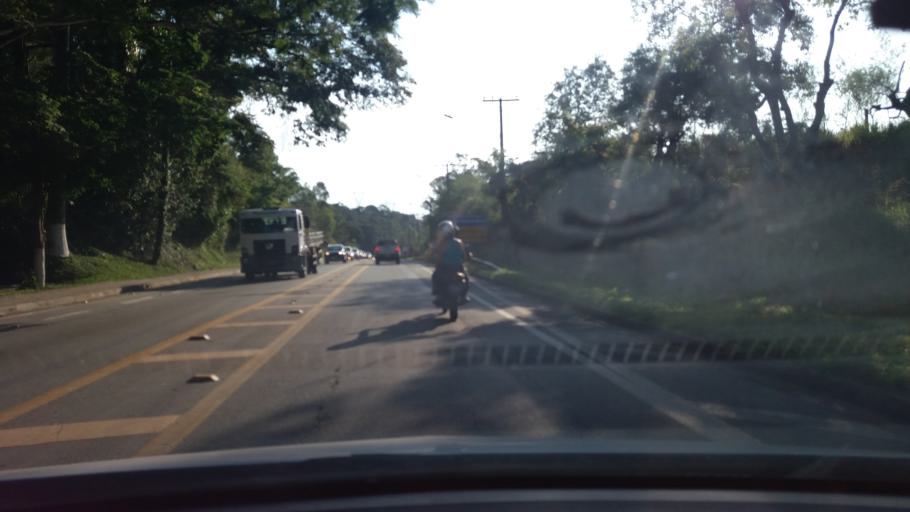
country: BR
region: Sao Paulo
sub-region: Mairipora
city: Mairipora
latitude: -23.3245
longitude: -46.5967
